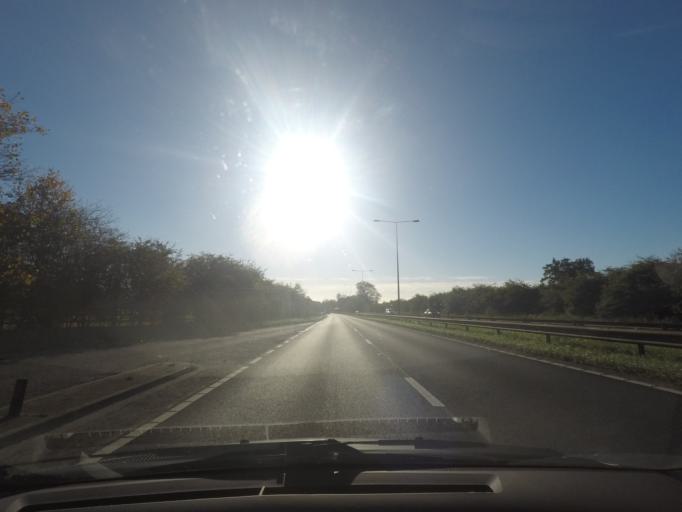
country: GB
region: England
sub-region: East Riding of Yorkshire
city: Welton
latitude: 53.7371
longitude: -0.5612
